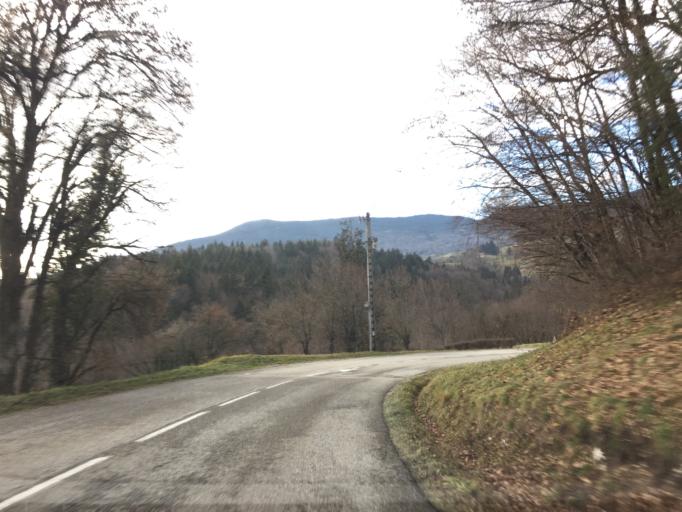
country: FR
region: Rhone-Alpes
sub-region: Departement de la Haute-Savoie
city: Gruffy
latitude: 45.7224
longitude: 6.1039
